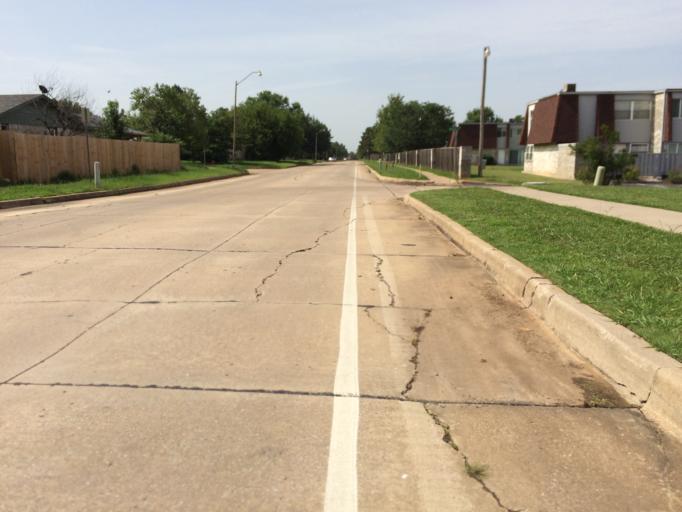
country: US
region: Oklahoma
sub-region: Cleveland County
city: Hall Park
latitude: 35.2176
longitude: -97.4165
